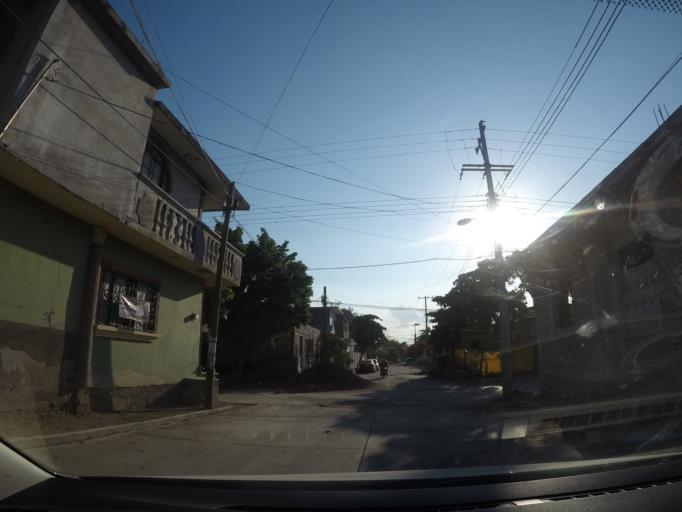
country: MX
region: Oaxaca
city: Juchitan de Zaragoza
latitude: 16.4345
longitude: -95.0263
